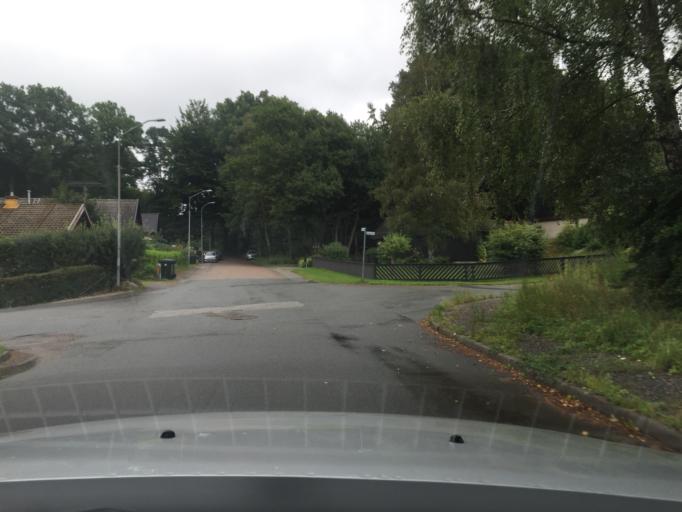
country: SE
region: Skane
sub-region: Hassleholms Kommun
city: Sosdala
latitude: 56.0035
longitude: 13.6367
